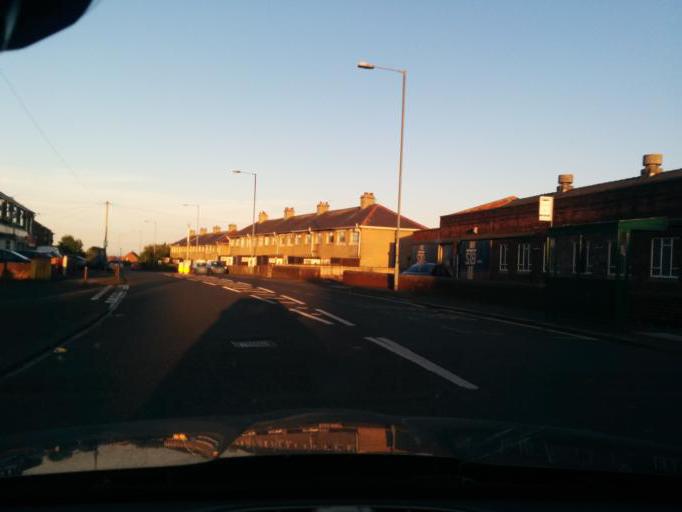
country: GB
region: England
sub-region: Northumberland
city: Newbiggin-by-the-Sea
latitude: 55.1880
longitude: -1.5206
